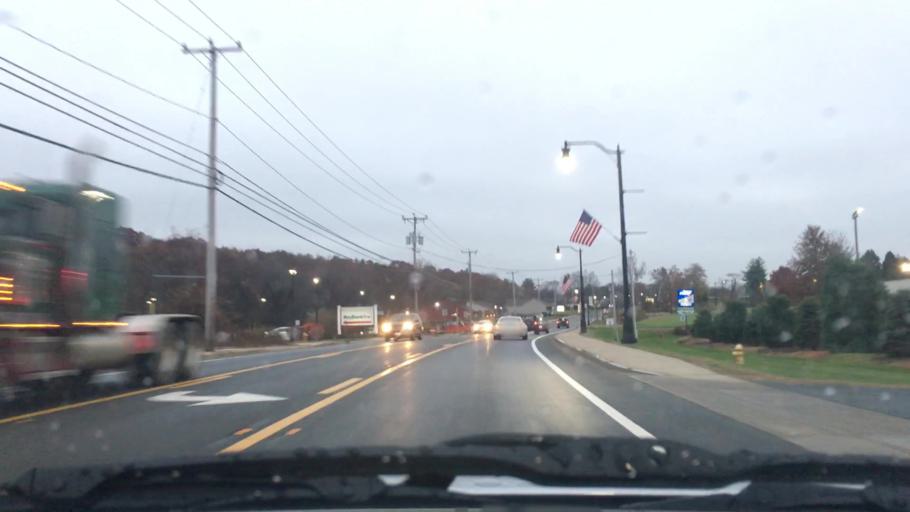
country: US
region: Massachusetts
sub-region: Hampden County
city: Southwick
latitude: 42.0697
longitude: -72.7644
